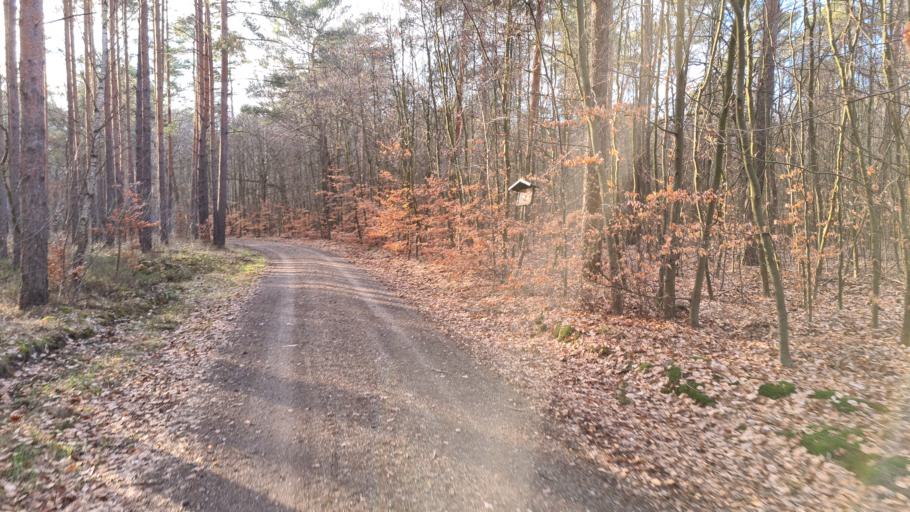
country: DE
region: Brandenburg
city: Schilda
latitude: 51.5807
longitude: 13.3171
